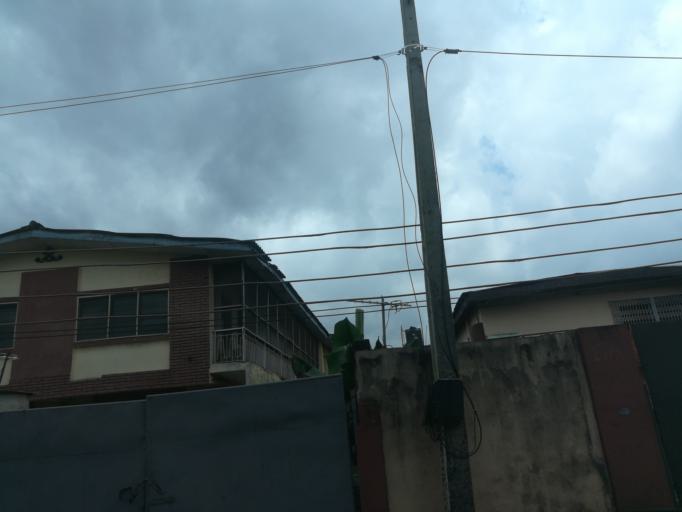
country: NG
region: Lagos
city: Somolu
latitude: 6.5545
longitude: 3.3643
